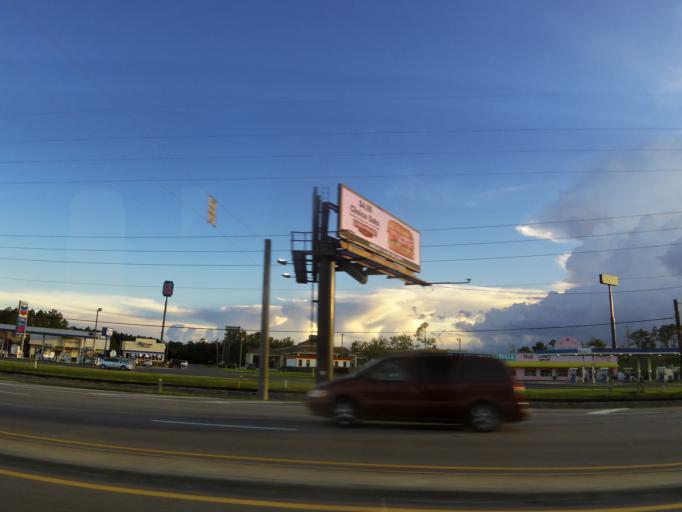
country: US
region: Georgia
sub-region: Camden County
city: Kingsland
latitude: 30.7901
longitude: -81.6567
